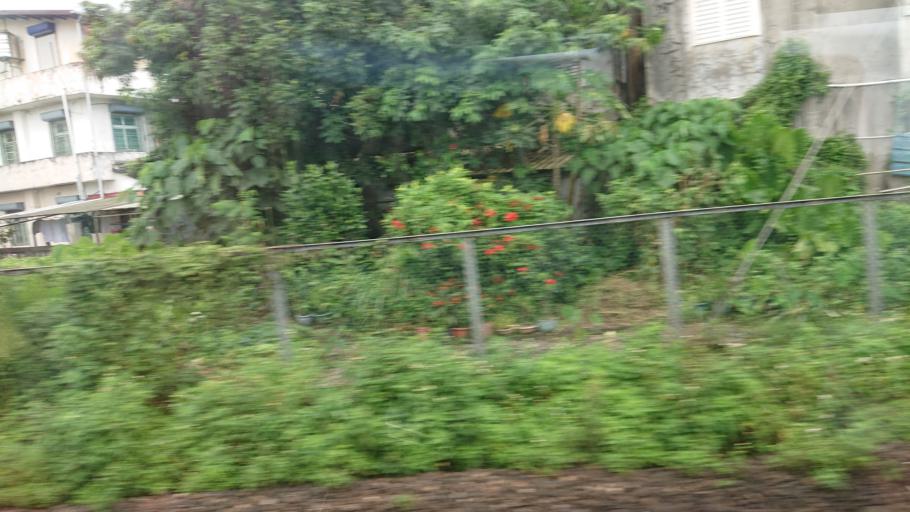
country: TW
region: Taiwan
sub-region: Yilan
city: Yilan
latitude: 24.8179
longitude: 121.7705
